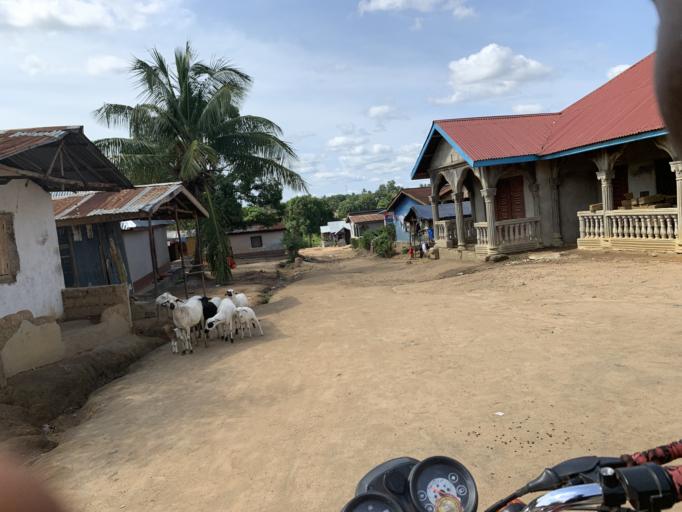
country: SL
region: Western Area
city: Waterloo
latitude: 8.3324
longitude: -13.0557
